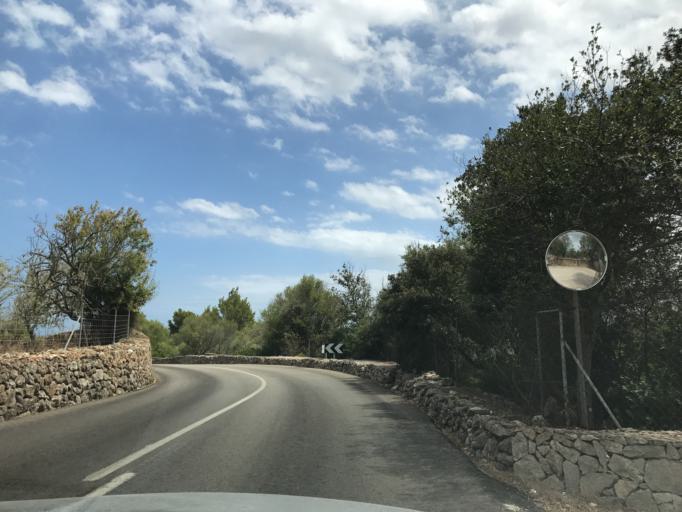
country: ES
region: Balearic Islands
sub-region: Illes Balears
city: Arta
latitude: 39.6606
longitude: 3.3352
